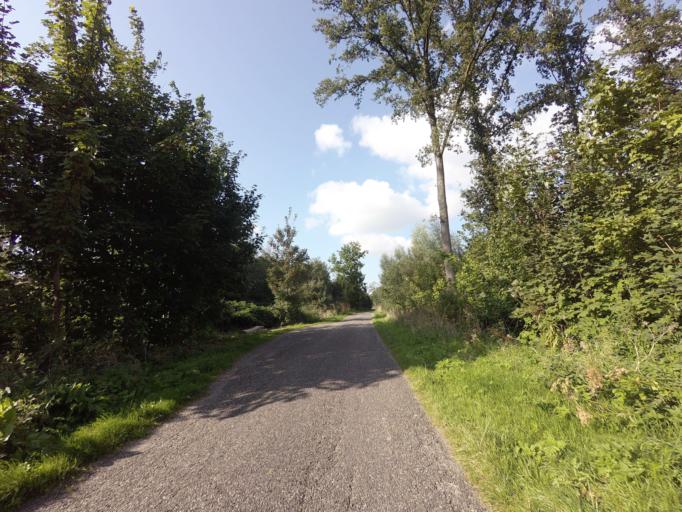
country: NL
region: Flevoland
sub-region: Gemeente Noordoostpolder
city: Ens
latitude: 52.6426
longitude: 5.7726
